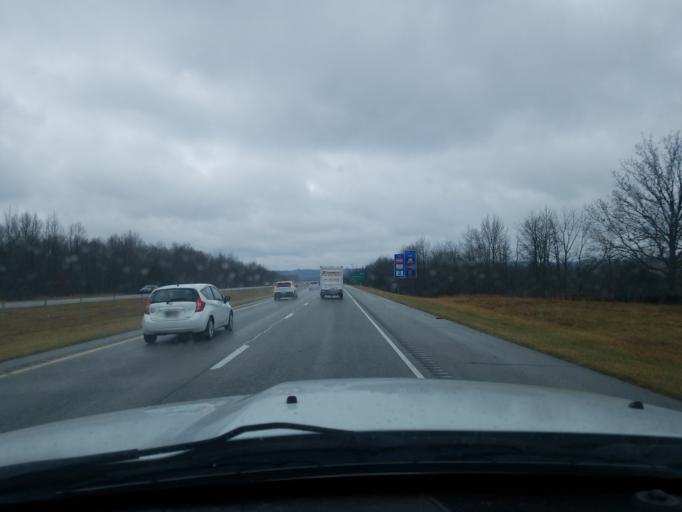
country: US
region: Indiana
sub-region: Clark County
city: Clarksville
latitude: 38.3452
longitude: -85.7791
